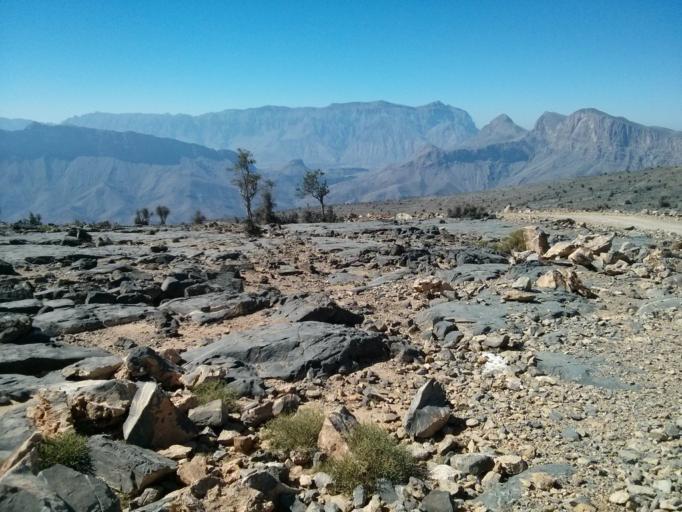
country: OM
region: Muhafazat ad Dakhiliyah
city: Bahla'
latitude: 23.1963
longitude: 57.1980
